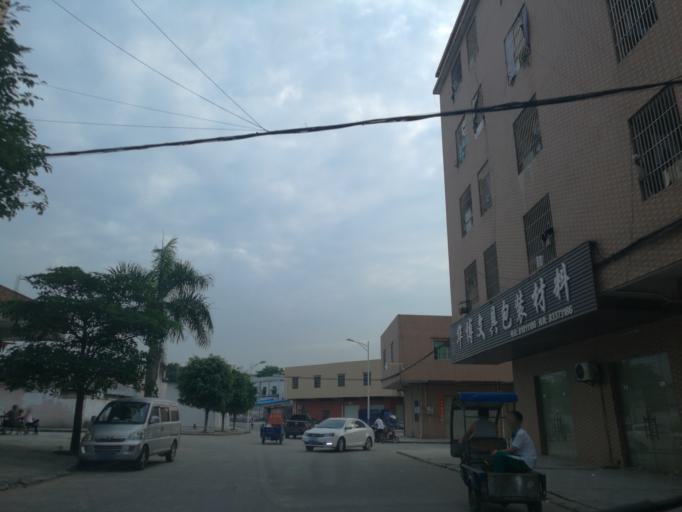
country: CN
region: Guangdong
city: Hengli
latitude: 23.0454
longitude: 113.9621
